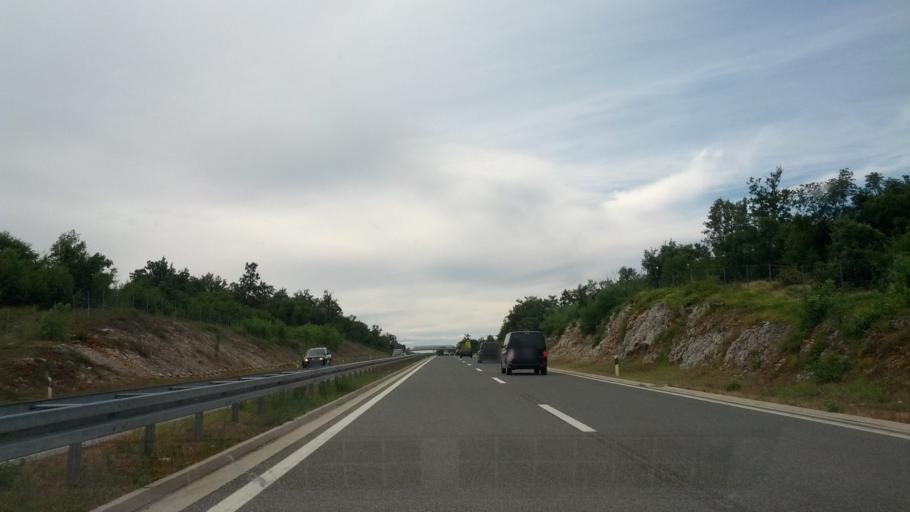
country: HR
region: Istarska
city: Vrsar
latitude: 45.1962
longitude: 13.7306
